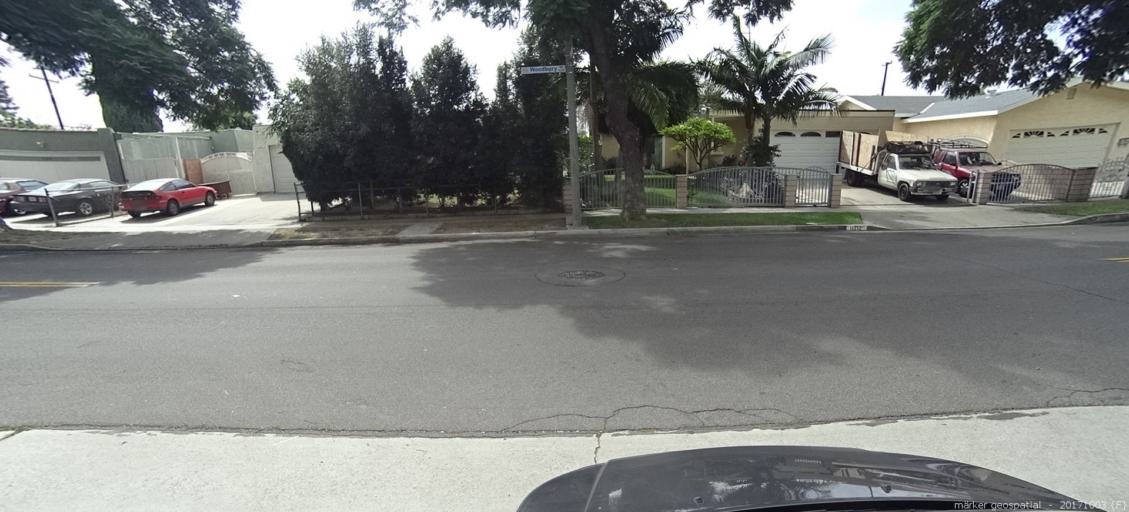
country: US
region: California
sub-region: Orange County
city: Garden Grove
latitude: 33.7638
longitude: -117.9339
